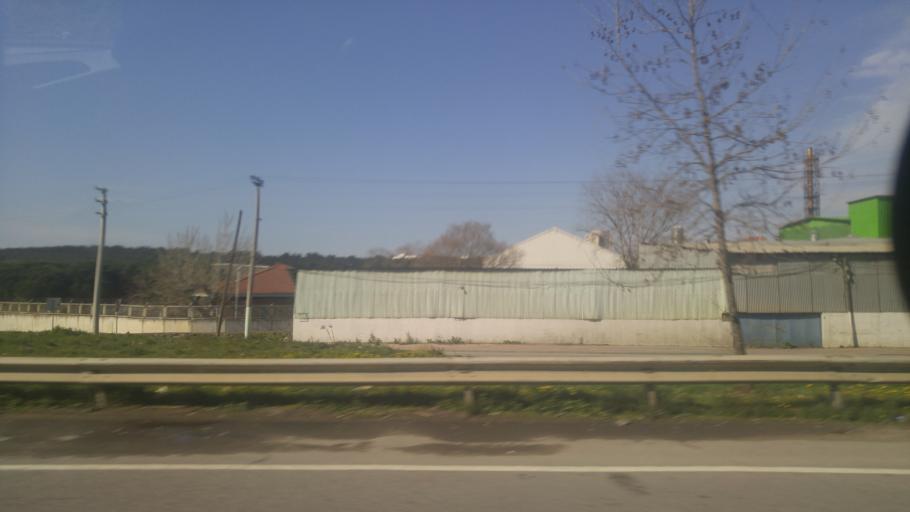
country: TR
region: Kocaeli
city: Darica
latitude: 40.8191
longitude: 29.3647
